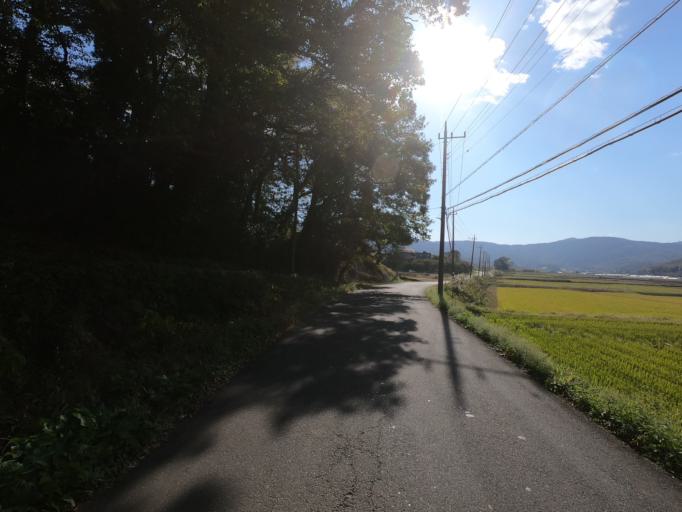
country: JP
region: Ibaraki
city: Ishioka
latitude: 36.1990
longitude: 140.1847
